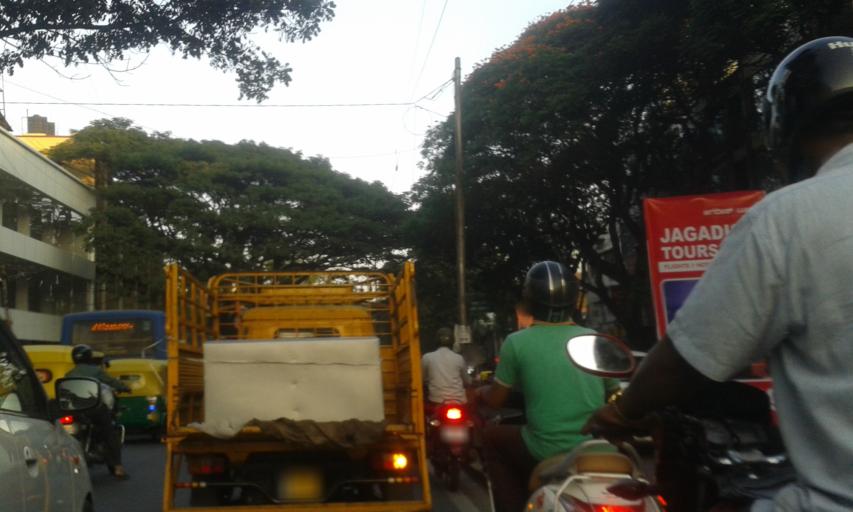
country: IN
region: Karnataka
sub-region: Bangalore Urban
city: Bangalore
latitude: 12.9169
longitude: 77.5944
